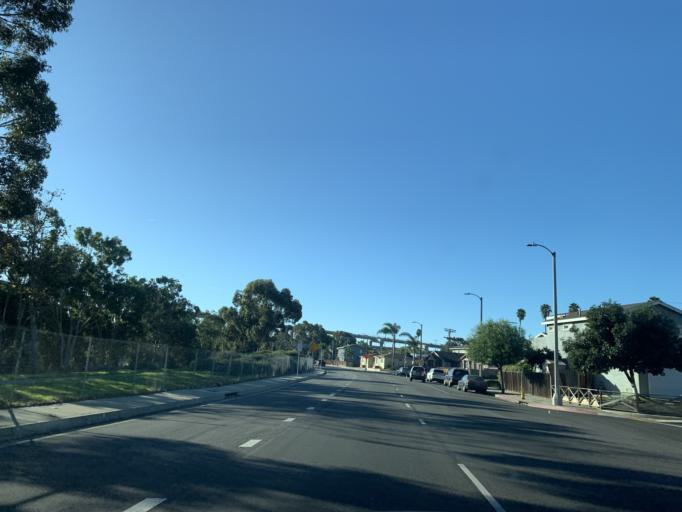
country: US
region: California
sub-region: Los Angeles County
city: Westmont
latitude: 33.9331
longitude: -118.2814
